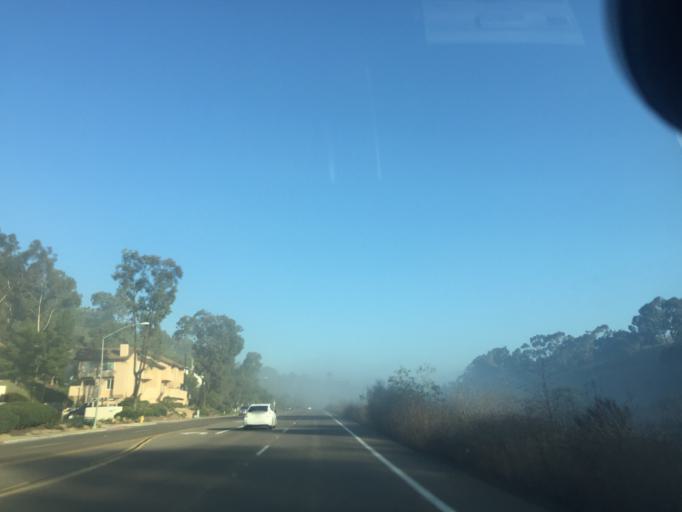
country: US
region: California
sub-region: San Diego County
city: La Jolla
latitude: 32.8558
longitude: -117.2371
